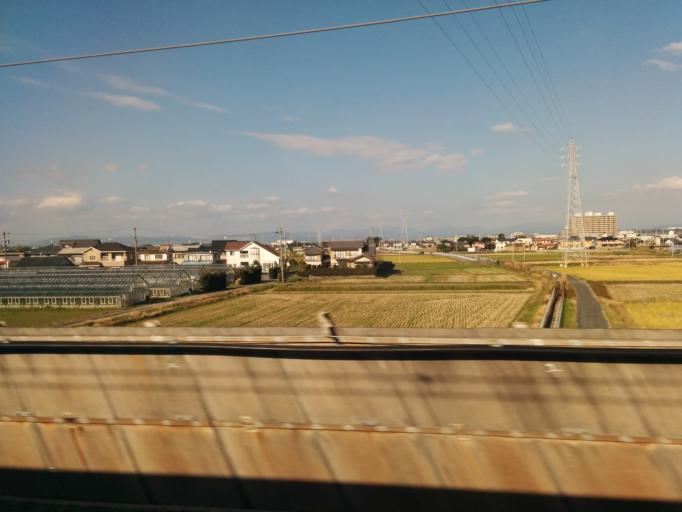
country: JP
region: Shizuoka
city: Iwata
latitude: 34.7028
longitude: 137.8188
